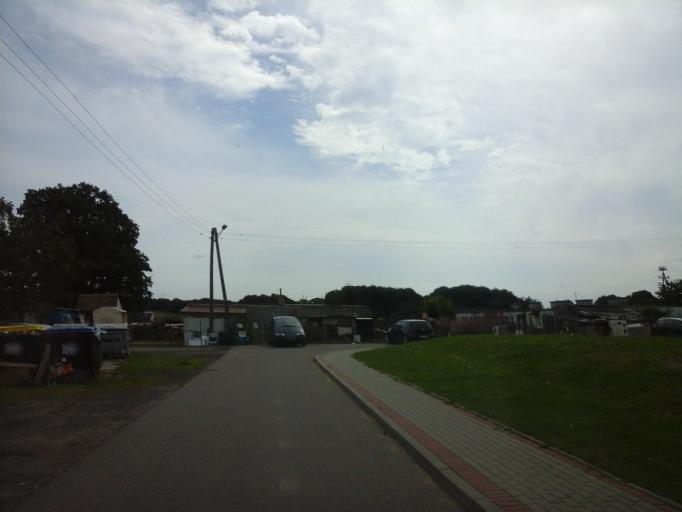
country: PL
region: West Pomeranian Voivodeship
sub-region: Powiat choszczenski
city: Recz
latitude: 53.2652
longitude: 15.6200
